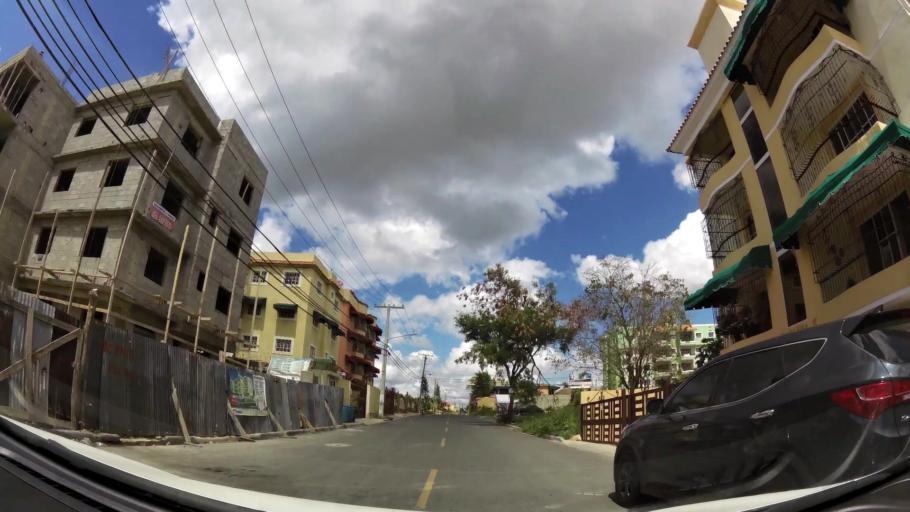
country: DO
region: Nacional
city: La Agustina
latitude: 18.5194
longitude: -69.9179
